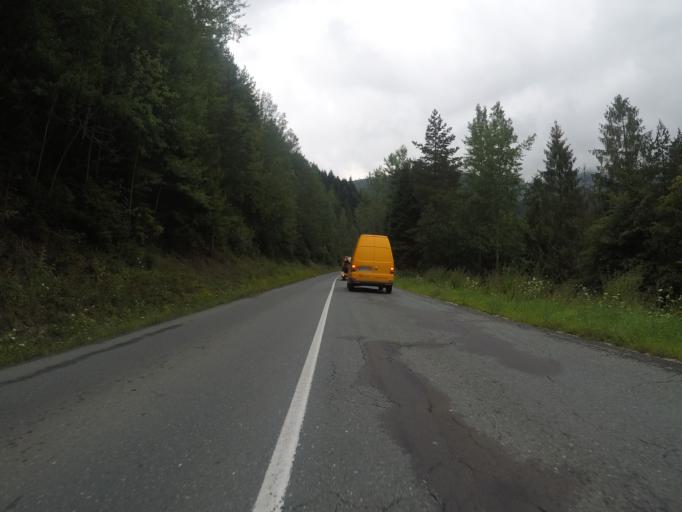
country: SK
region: Kosicky
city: Spisska Nova Ves
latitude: 48.8951
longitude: 20.5204
